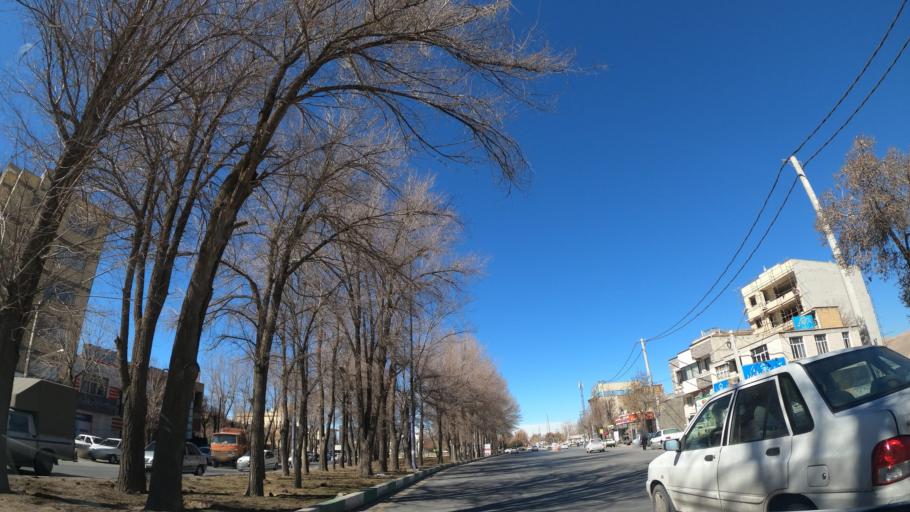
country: IR
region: Chahar Mahall va Bakhtiari
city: Shahrekord
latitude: 32.3113
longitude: 50.8860
